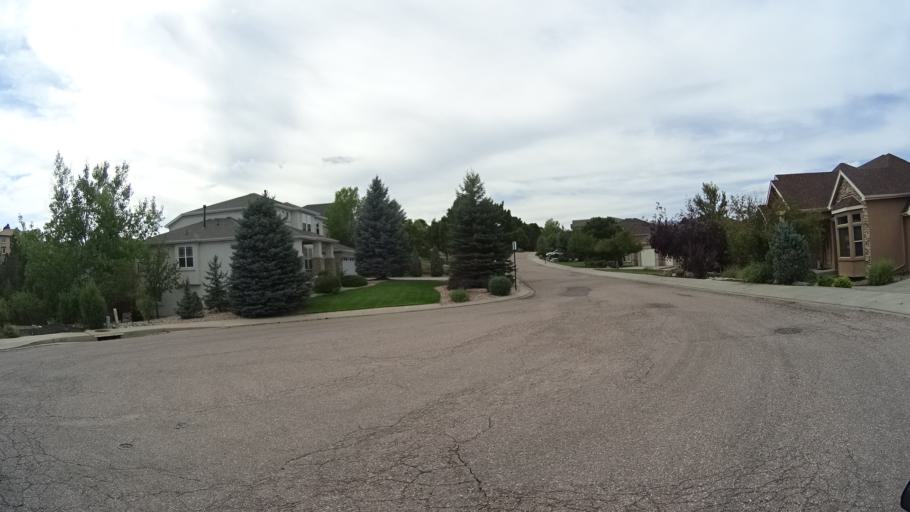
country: US
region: Colorado
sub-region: El Paso County
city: Colorado Springs
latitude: 38.9001
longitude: -104.7864
